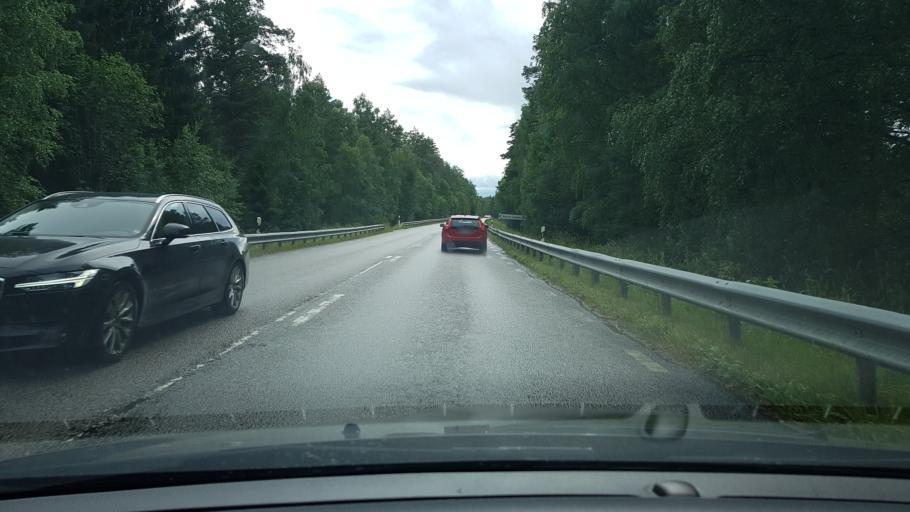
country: SE
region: Uppsala
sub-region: Uppsala Kommun
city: Saevja
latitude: 59.7945
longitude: 17.6775
